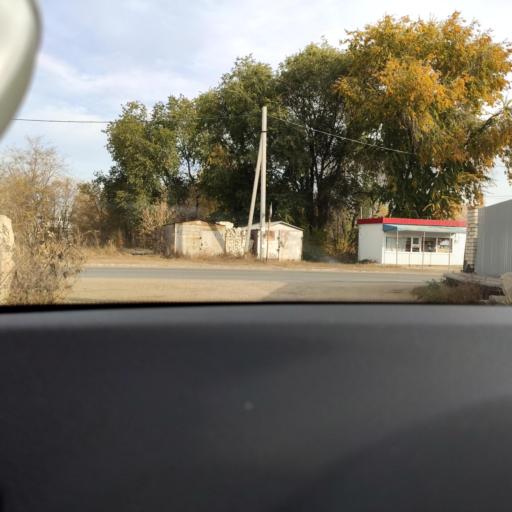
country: RU
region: Samara
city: Samara
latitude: 53.1846
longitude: 50.2298
